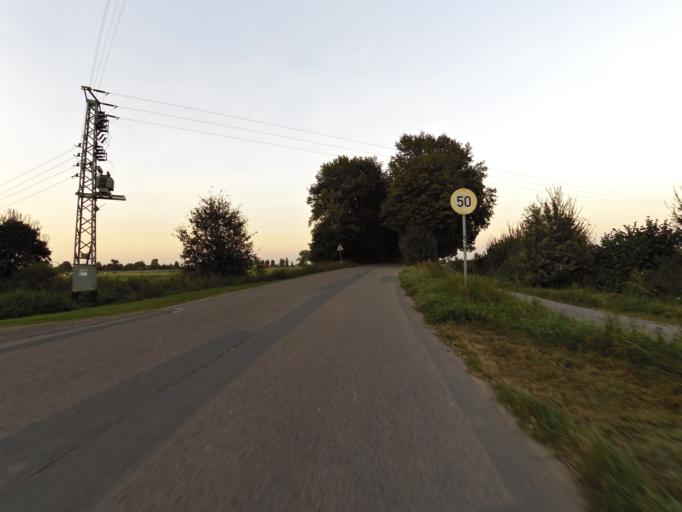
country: NL
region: Gelderland
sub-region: Gemeente Montferland
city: s-Heerenberg
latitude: 51.8584
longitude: 6.2674
